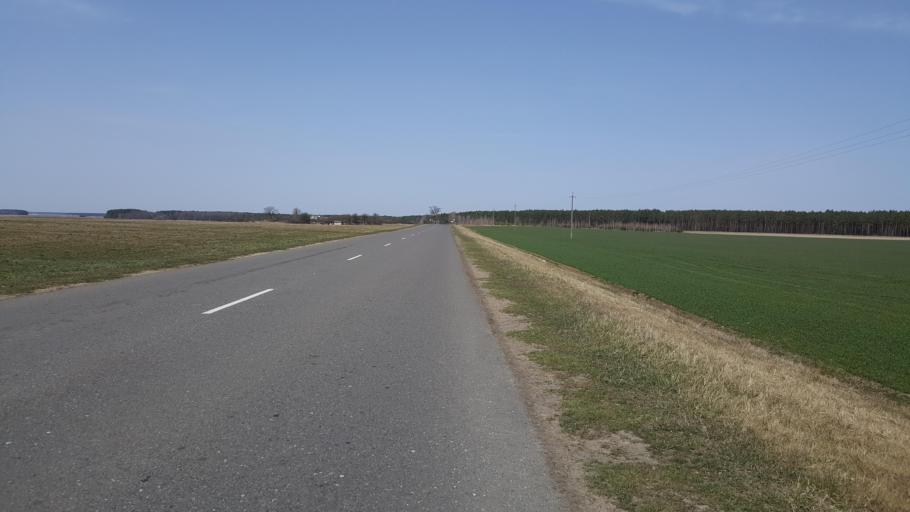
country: BY
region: Brest
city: Kamyanyuki
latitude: 52.4972
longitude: 23.6734
